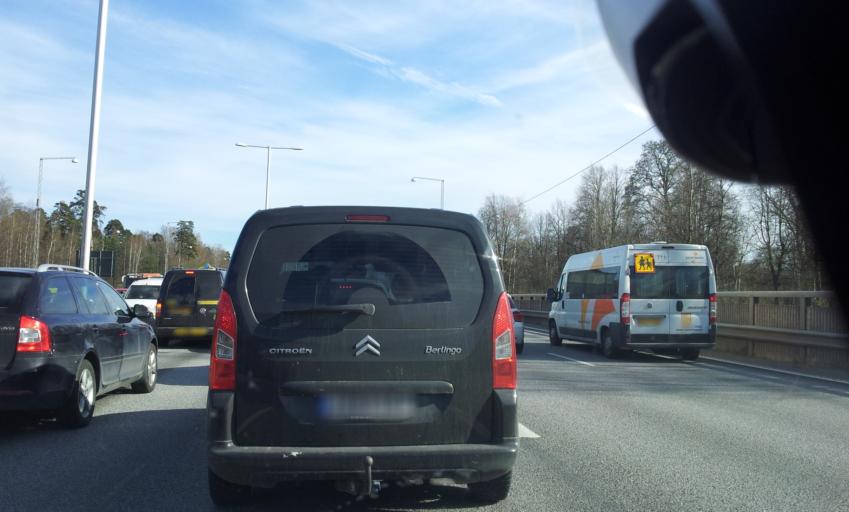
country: SE
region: Stockholm
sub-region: Norrtalje Kommun
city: Bergshamra
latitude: 59.3583
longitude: 18.0296
